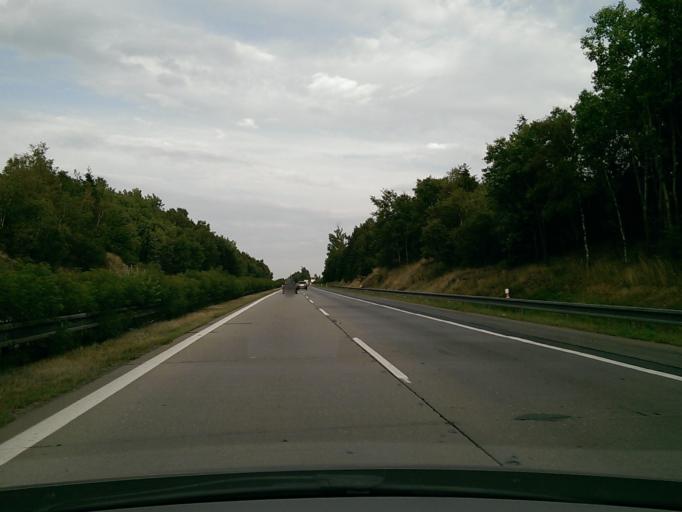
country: CZ
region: Vysocina
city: Kamenice
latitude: 49.4086
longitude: 15.7699
